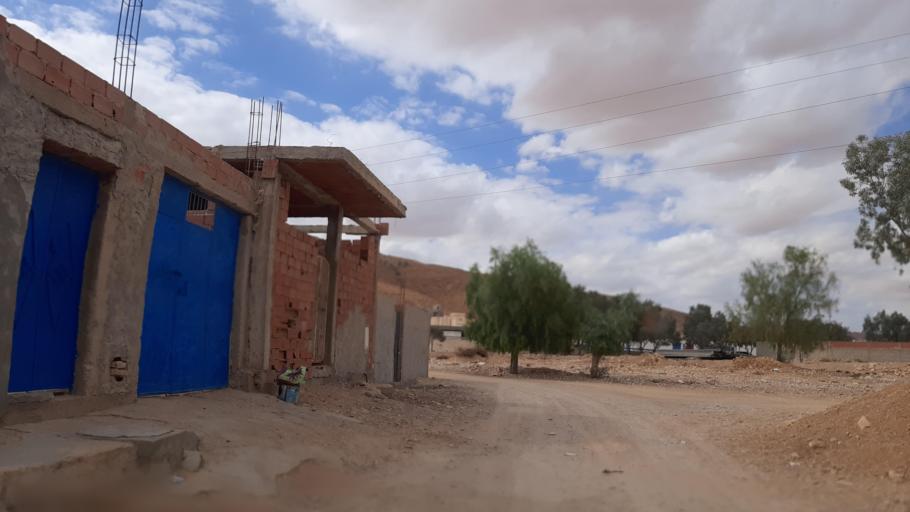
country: TN
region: Tataouine
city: Tataouine
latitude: 32.9437
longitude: 10.4551
